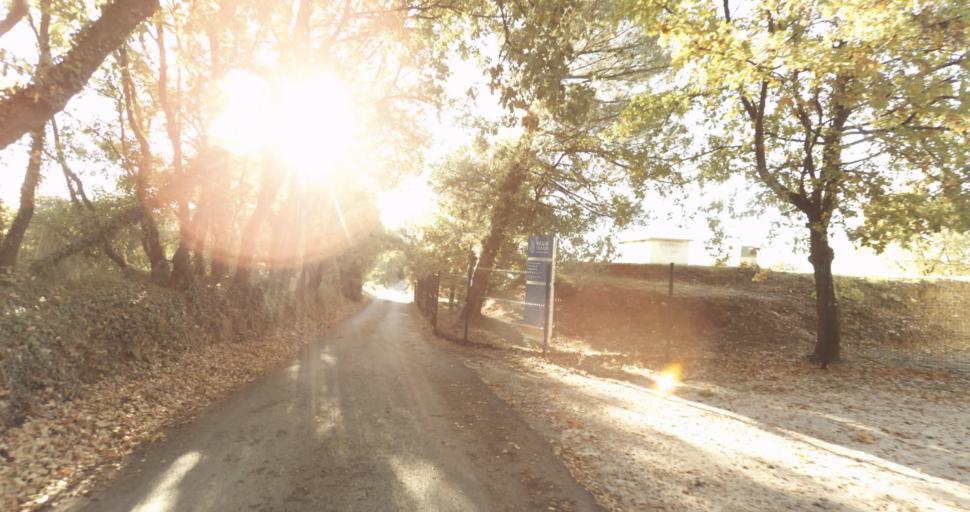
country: FR
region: Provence-Alpes-Cote d'Azur
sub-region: Departement des Bouches-du-Rhone
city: Venelles
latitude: 43.6041
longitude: 5.4740
